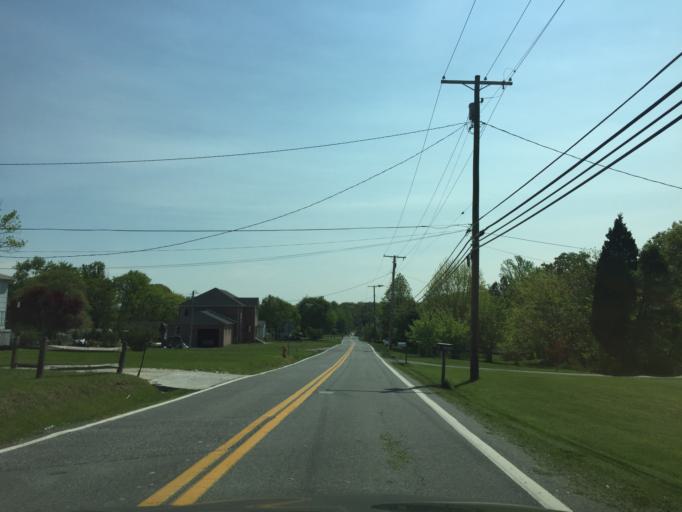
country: US
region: Maryland
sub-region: Baltimore County
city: White Marsh
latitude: 39.3660
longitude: -76.4218
